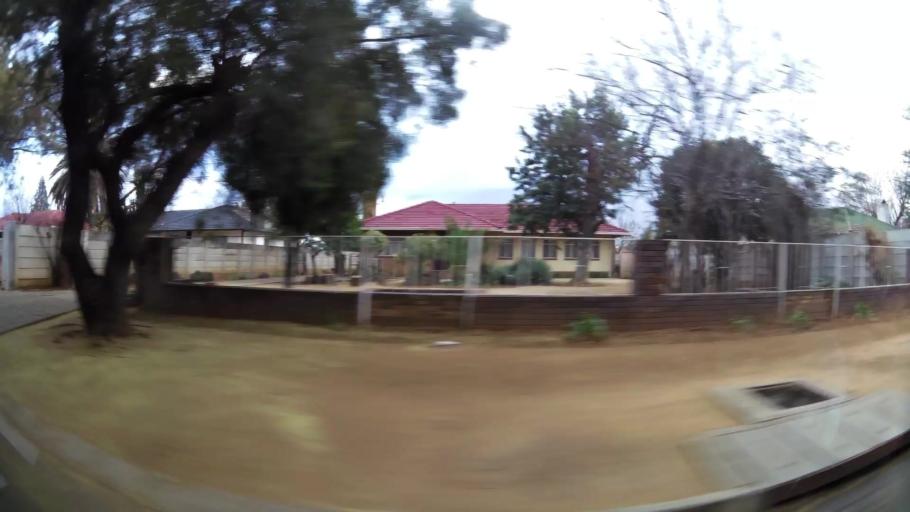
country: ZA
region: Orange Free State
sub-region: Lejweleputswa District Municipality
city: Welkom
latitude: -27.9564
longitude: 26.7266
